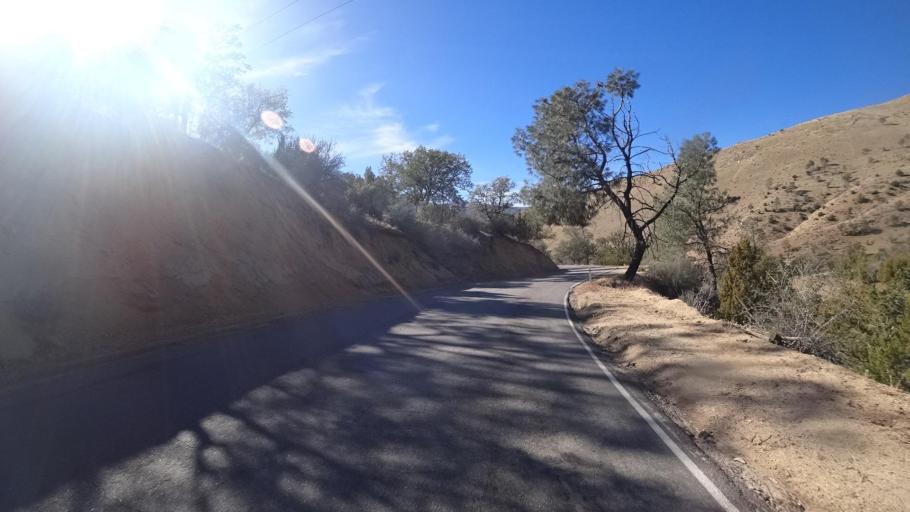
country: US
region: California
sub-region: Kern County
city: Bodfish
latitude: 35.5606
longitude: -118.5062
